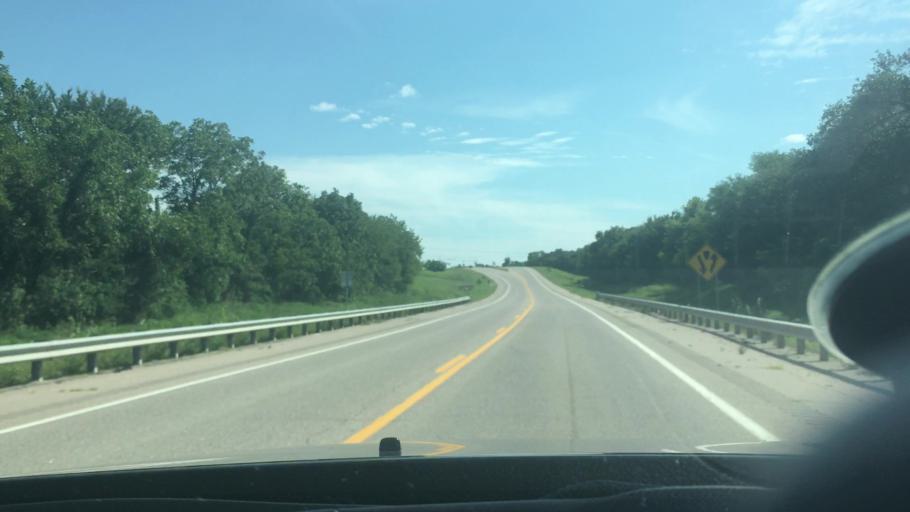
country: US
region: Oklahoma
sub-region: Seminole County
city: Konawa
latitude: 34.9476
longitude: -96.6809
